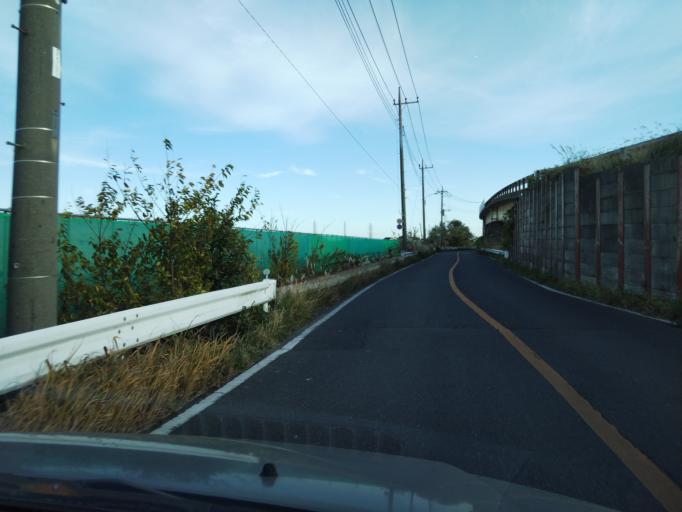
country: JP
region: Saitama
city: Yoshikawa
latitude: 35.8705
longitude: 139.8557
